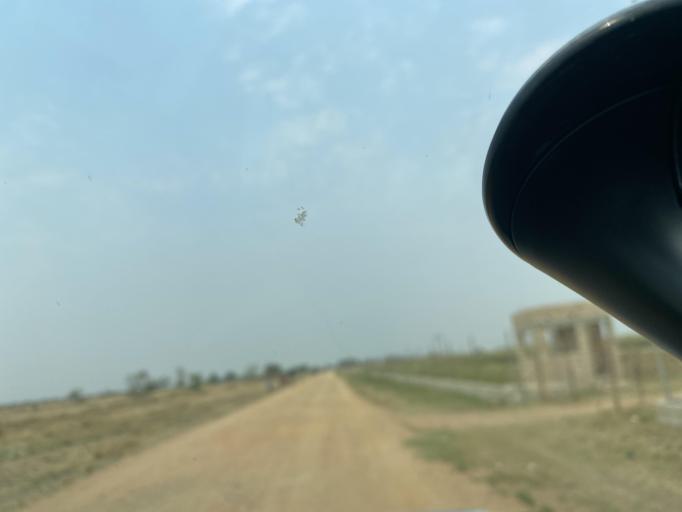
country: ZM
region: Lusaka
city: Kafue
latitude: -15.6802
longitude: 28.0120
